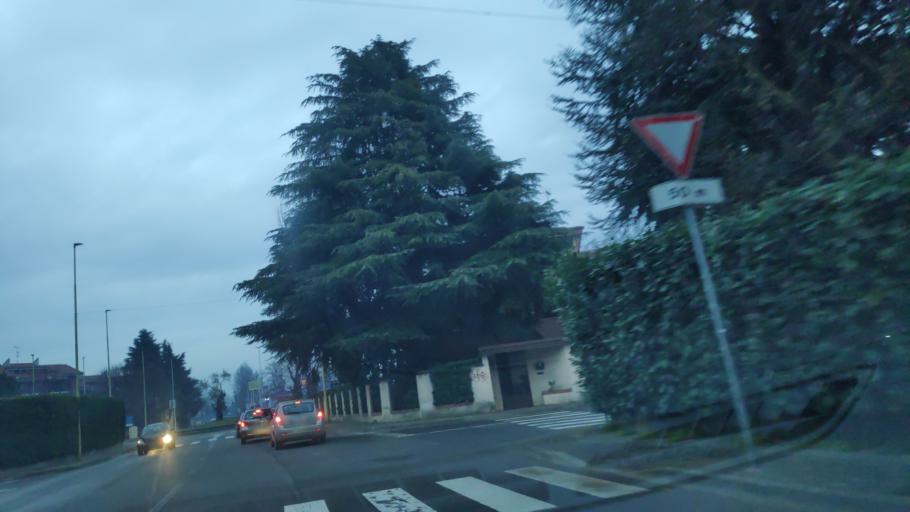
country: IT
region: Lombardy
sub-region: Citta metropolitana di Milano
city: Romano Banco
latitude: 45.4254
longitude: 9.1248
